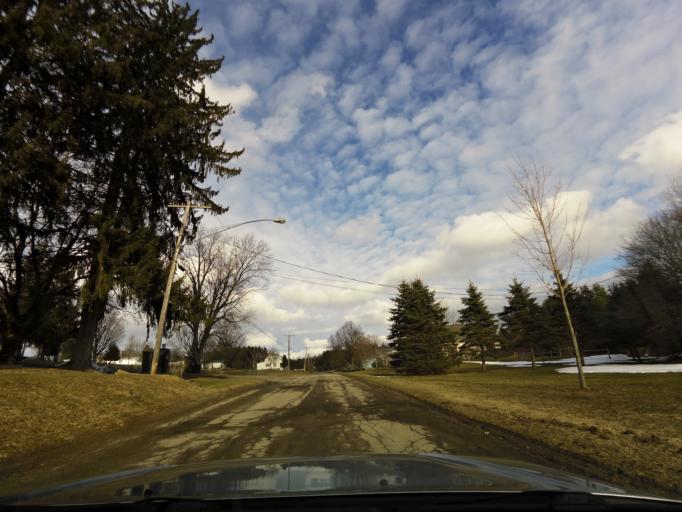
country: US
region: New York
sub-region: Cattaraugus County
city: Franklinville
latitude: 42.3373
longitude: -78.4497
